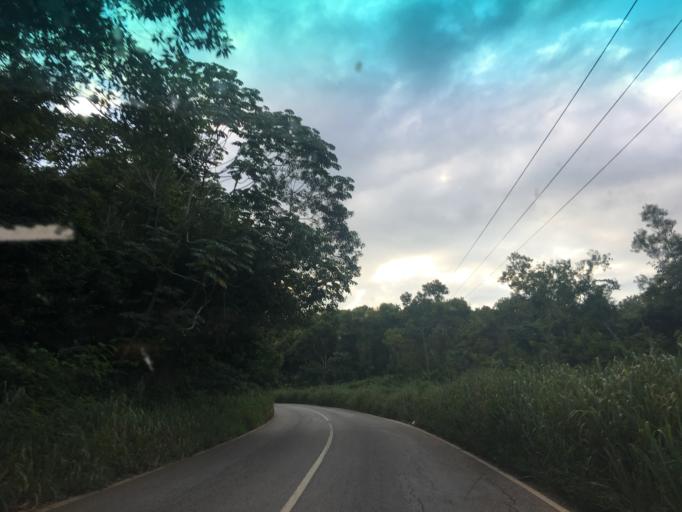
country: GH
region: Western
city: Bibiani
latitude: 6.4648
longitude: -2.3297
